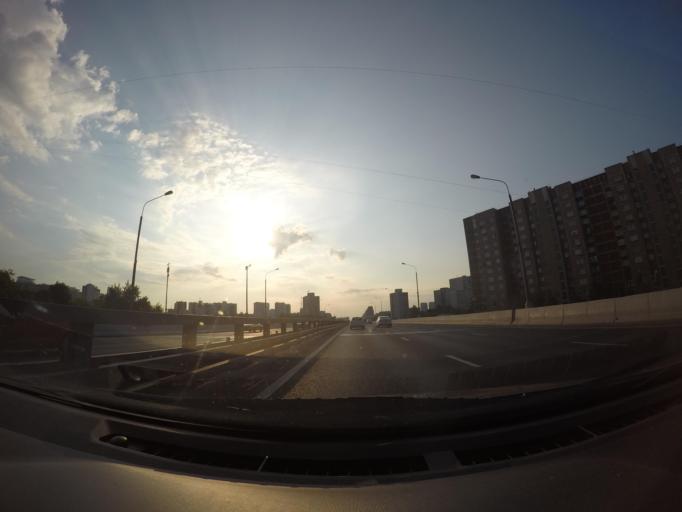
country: RU
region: Moscow
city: Tekstil'shchiki
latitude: 55.7086
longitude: 37.7417
